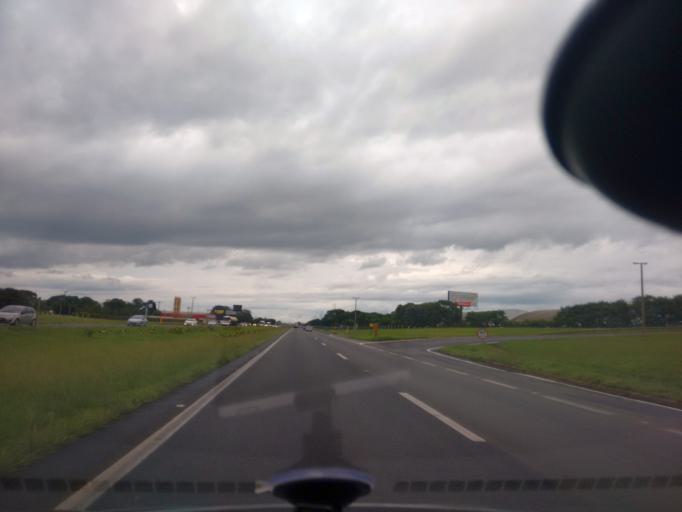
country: BR
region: Sao Paulo
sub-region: Rio Claro
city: Rio Claro
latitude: -22.4344
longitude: -47.5701
